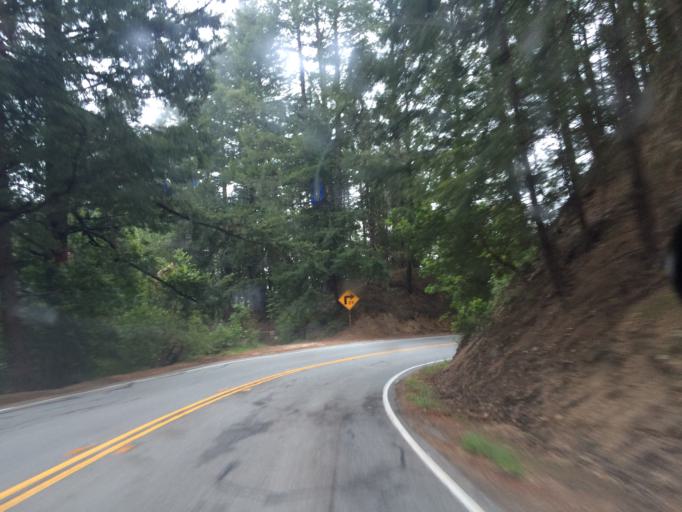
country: US
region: California
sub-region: Santa Cruz County
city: Boulder Creek
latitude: 37.2355
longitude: -122.1457
